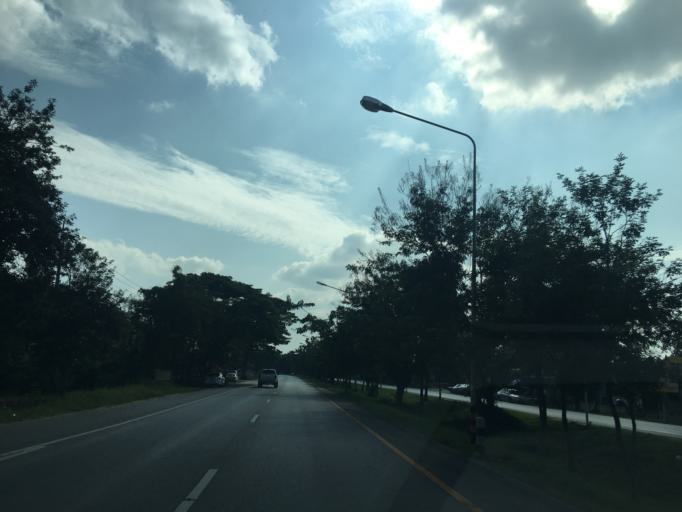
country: TH
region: Chiang Rai
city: Mae Lao
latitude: 19.7687
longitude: 99.7370
